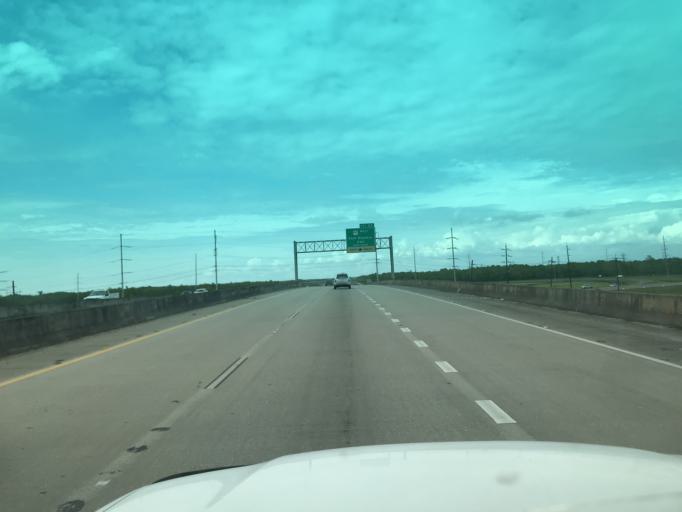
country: US
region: Louisiana
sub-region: Saint Bernard Parish
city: Chalmette
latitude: 30.0252
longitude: -89.9393
